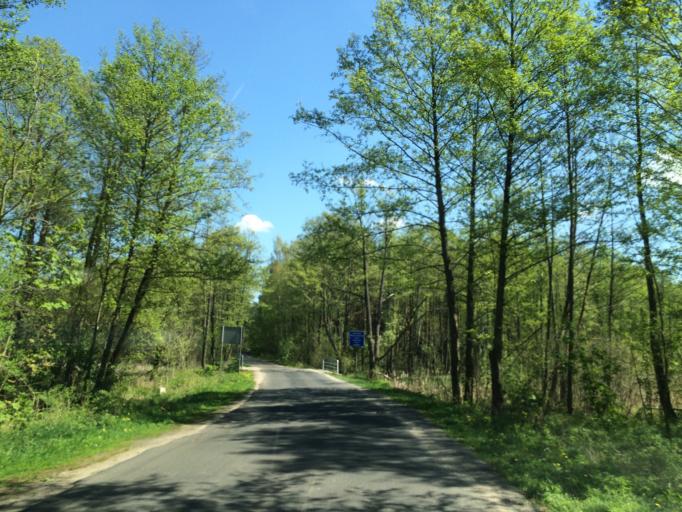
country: PL
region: Kujawsko-Pomorskie
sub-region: Powiat brodnicki
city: Brodnica
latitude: 53.3843
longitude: 19.4139
